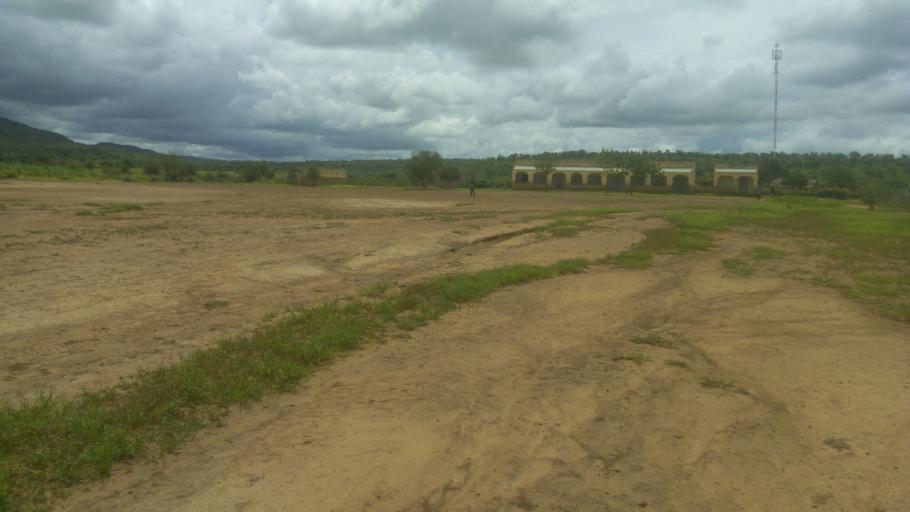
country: ML
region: Kayes
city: Yelimane
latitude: 14.6266
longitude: -10.7246
